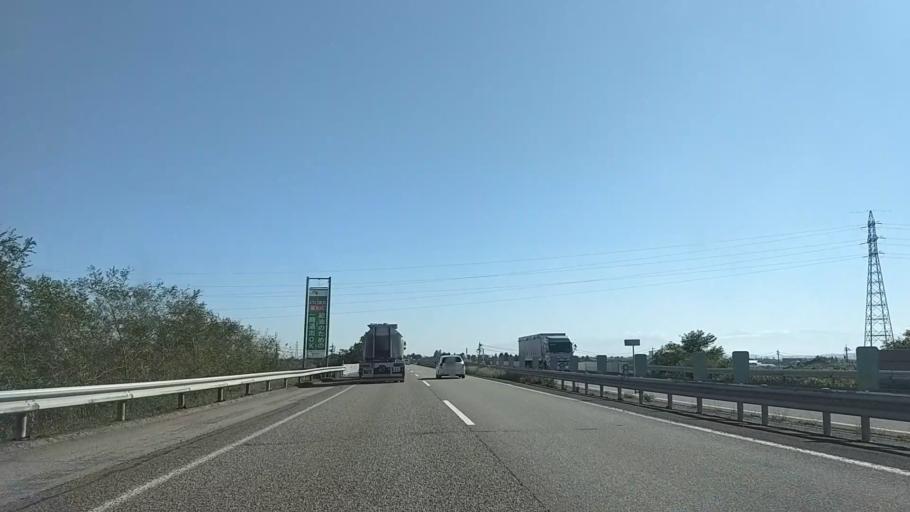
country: JP
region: Toyama
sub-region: Oyabe Shi
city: Oyabe
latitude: 36.6287
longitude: 136.8817
